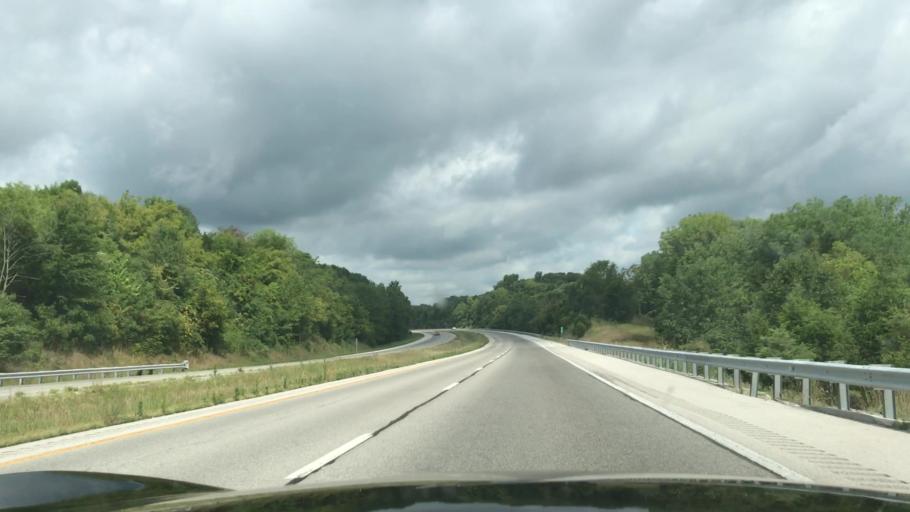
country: US
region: Kentucky
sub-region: Warren County
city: Bowling Green
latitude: 37.0307
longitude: -86.5393
